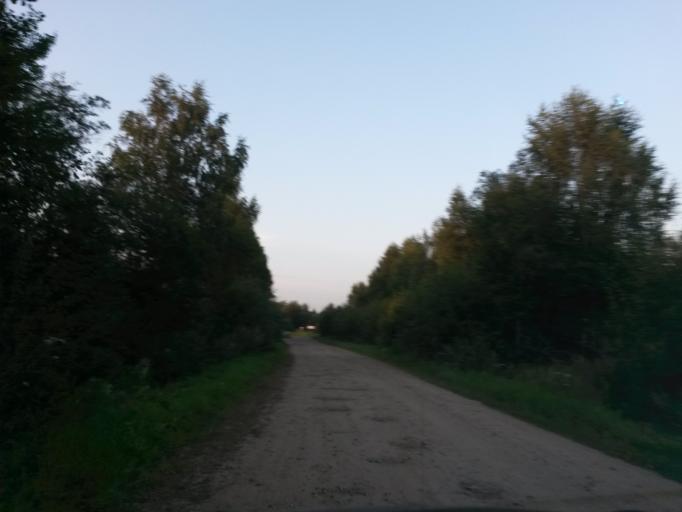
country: RU
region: Jaroslavl
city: Tutayev
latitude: 57.9479
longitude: 39.4565
